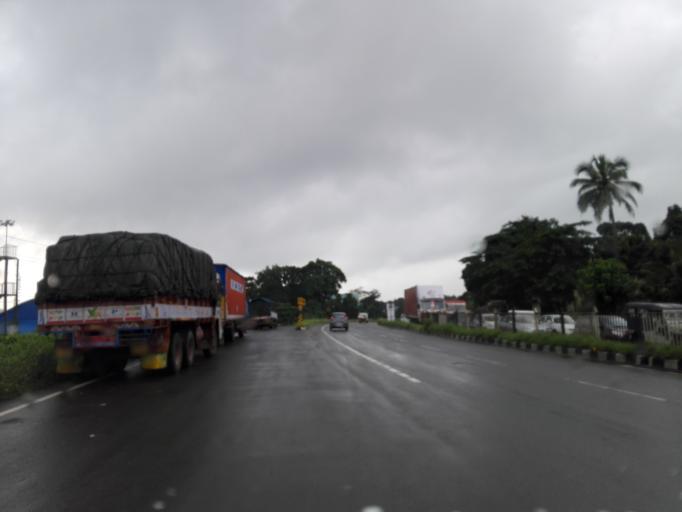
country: IN
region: Kerala
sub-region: Ernakulam
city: Elur
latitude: 10.0711
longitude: 76.3175
